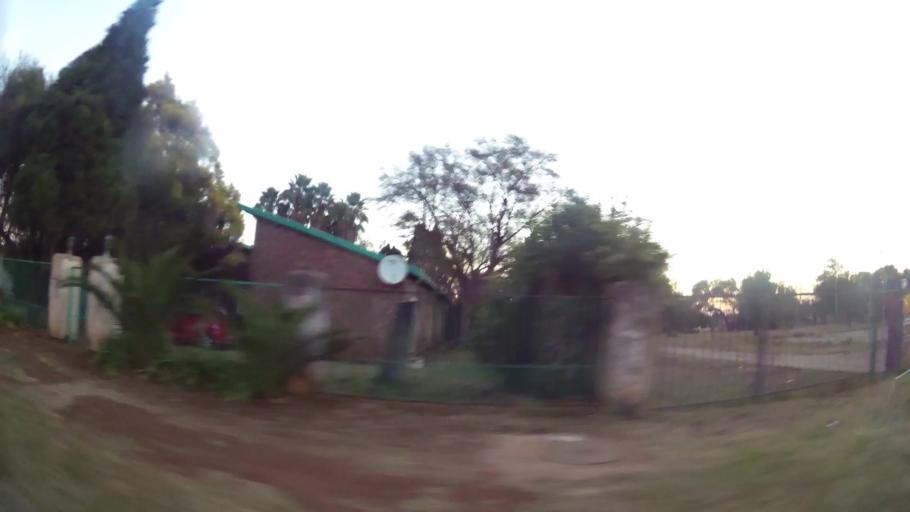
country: ZA
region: Gauteng
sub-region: City of Tshwane Metropolitan Municipality
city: Centurion
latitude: -25.8548
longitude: 28.1336
